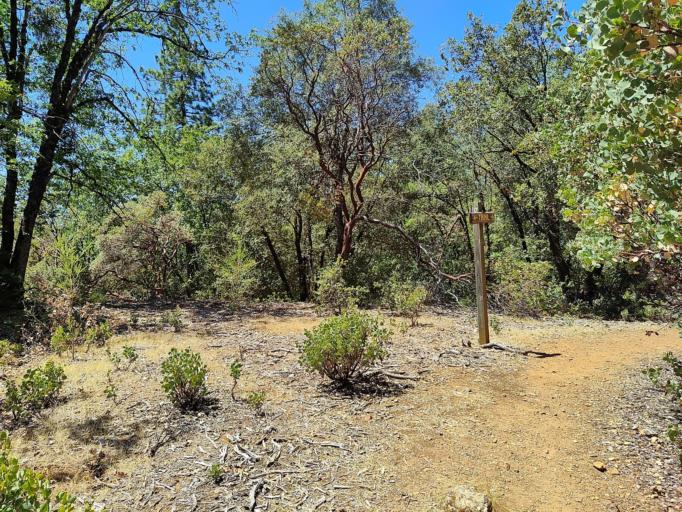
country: US
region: California
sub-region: Placer County
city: Meadow Vista
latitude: 39.0346
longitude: -120.9842
